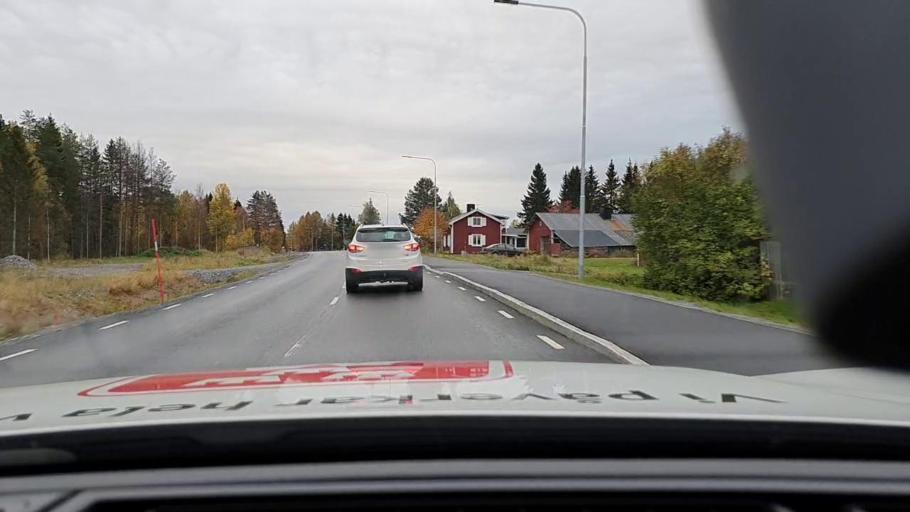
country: SE
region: Norrbotten
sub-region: Bodens Kommun
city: Saevast
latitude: 65.7748
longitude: 21.6952
